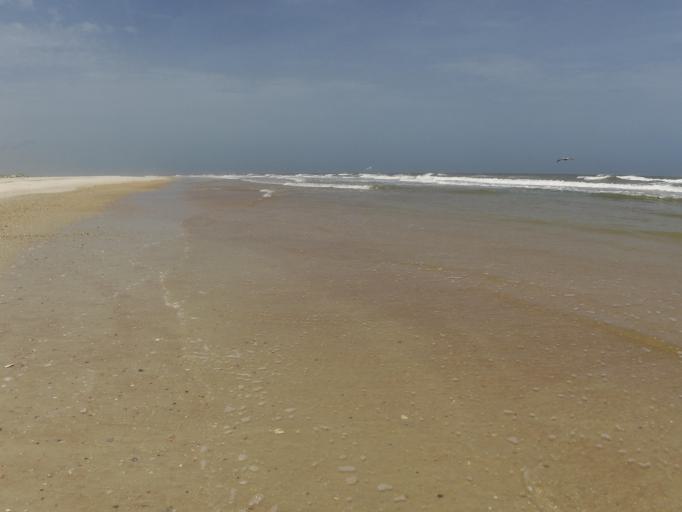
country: US
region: Florida
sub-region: Saint Johns County
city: Saint Augustine
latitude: 29.9018
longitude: -81.2770
